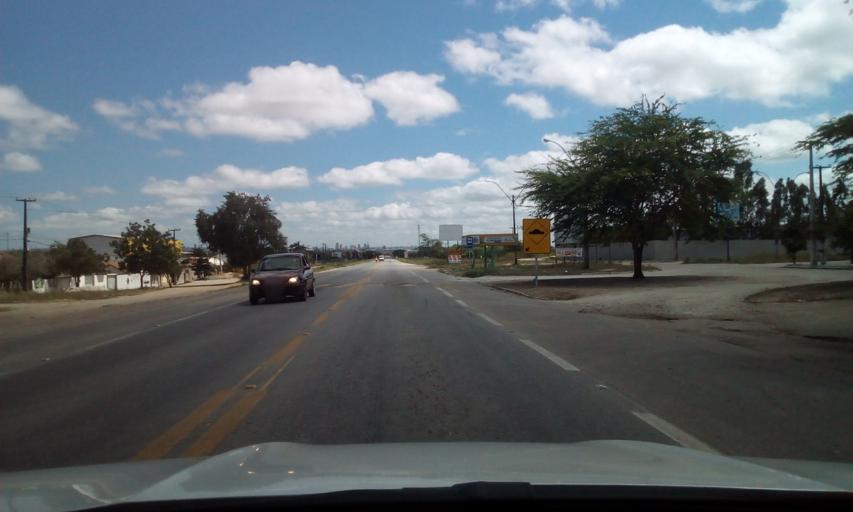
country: BR
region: Paraiba
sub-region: Campina Grande
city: Campina Grande
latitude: -7.3033
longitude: -35.8926
